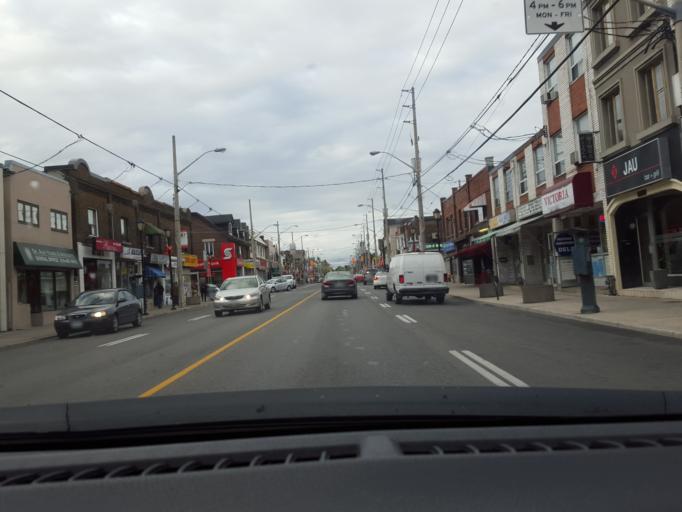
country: CA
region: Ontario
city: Toronto
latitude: 43.6879
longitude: -79.3482
